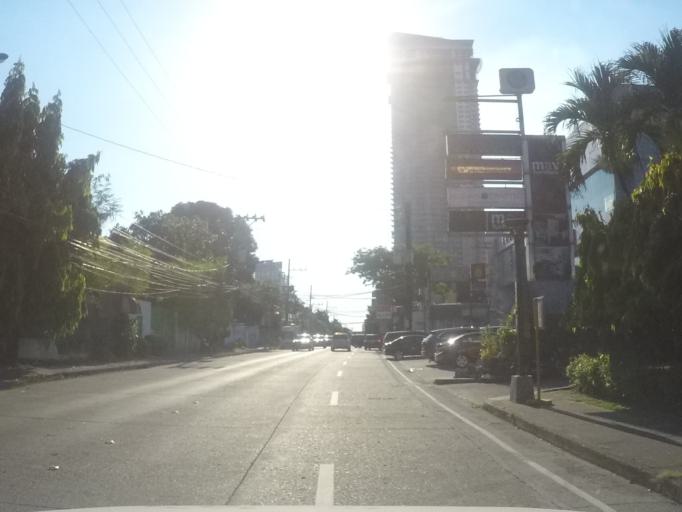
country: PH
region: Metro Manila
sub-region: Pasig
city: Pasig City
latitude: 14.6009
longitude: 121.0556
